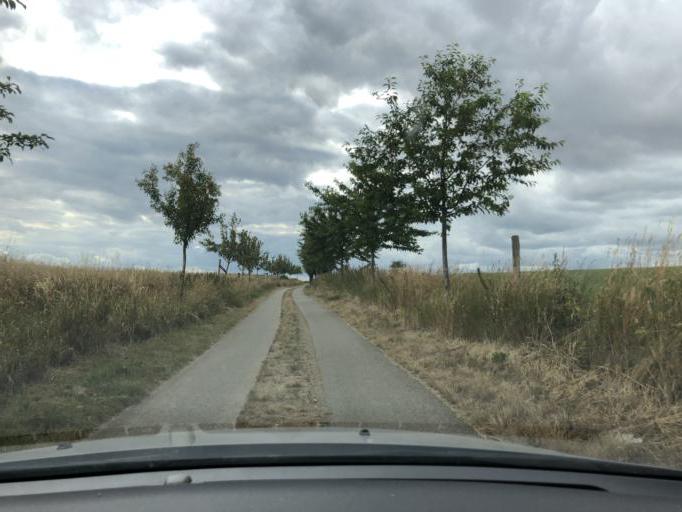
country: DE
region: Saxony
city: Geithain
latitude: 51.0209
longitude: 12.6488
